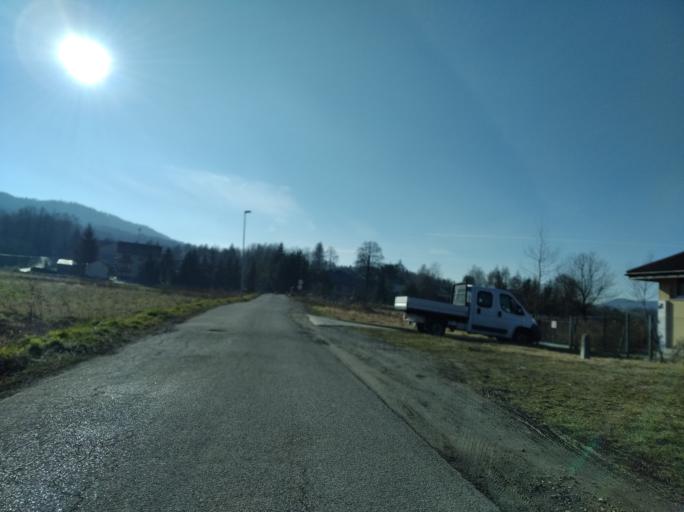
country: PL
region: Subcarpathian Voivodeship
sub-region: Powiat strzyzowski
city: Jawornik
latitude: 49.8049
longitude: 21.8887
